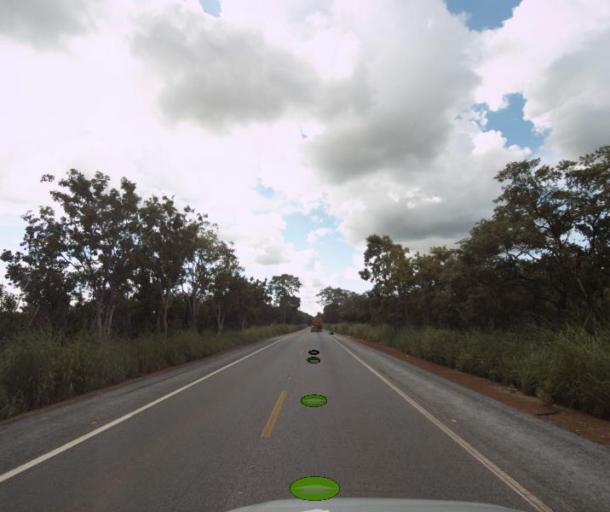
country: BR
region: Goias
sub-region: Porangatu
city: Porangatu
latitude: -13.1756
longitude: -49.1706
